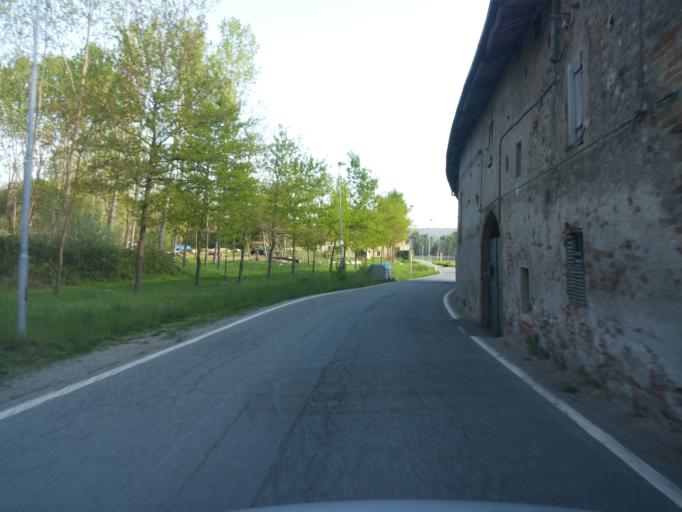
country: IT
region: Piedmont
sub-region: Provincia di Torino
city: Azeglio
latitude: 45.4242
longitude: 7.9729
